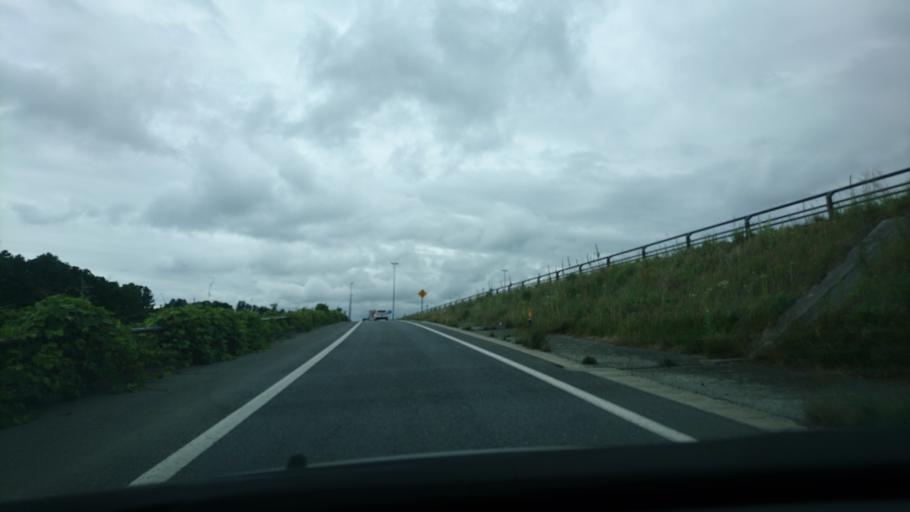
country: JP
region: Miyagi
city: Wakuya
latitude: 38.6752
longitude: 141.2660
